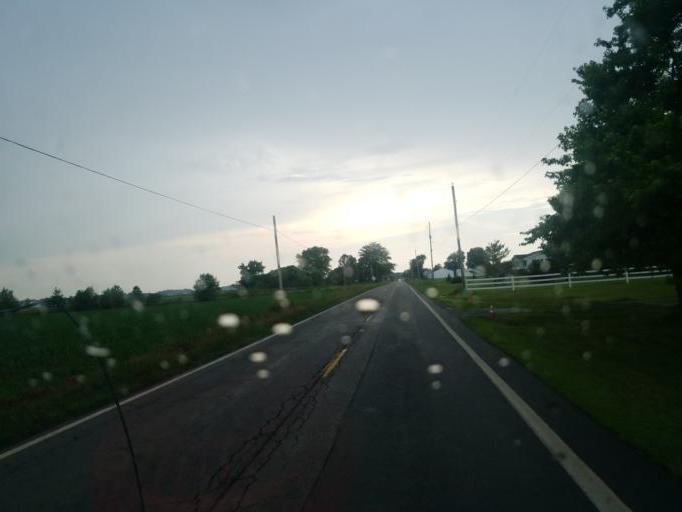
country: US
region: Ohio
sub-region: Wayne County
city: Rittman
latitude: 40.9457
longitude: -81.8153
